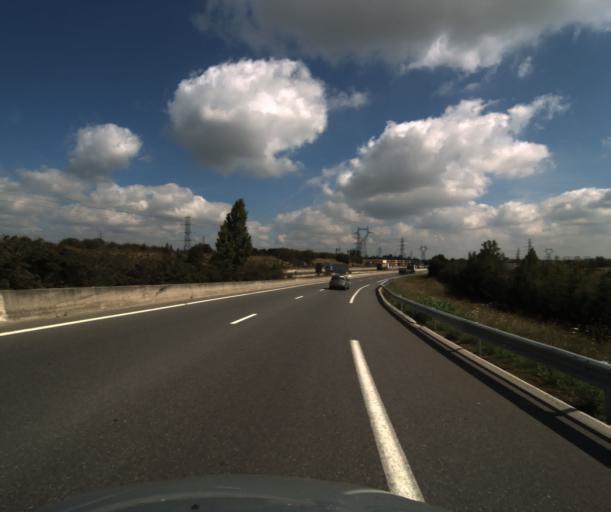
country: FR
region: Midi-Pyrenees
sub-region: Departement de la Haute-Garonne
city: Pinsaguel
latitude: 43.5197
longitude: 1.3775
